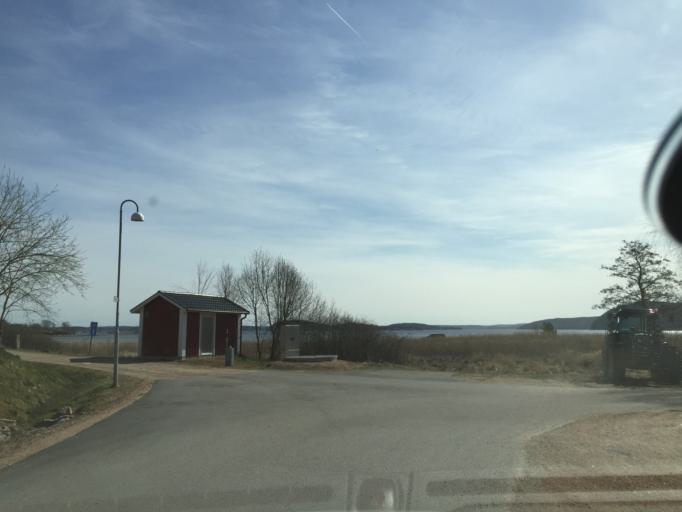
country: SE
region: Vaestra Goetaland
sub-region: Orust
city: Henan
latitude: 58.3423
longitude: 11.7308
